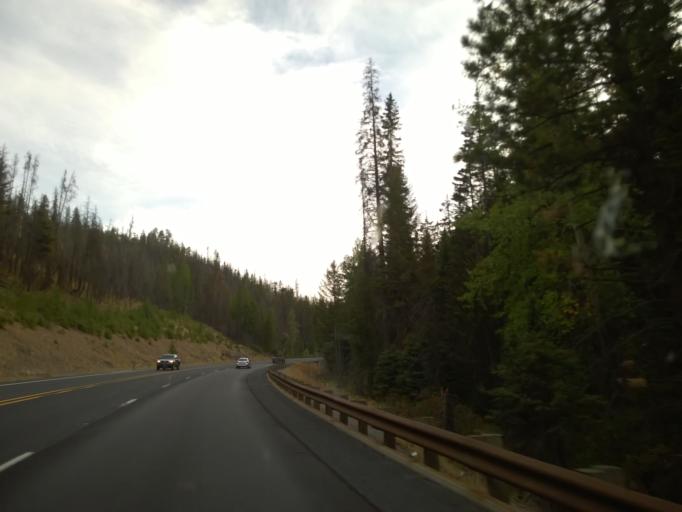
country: US
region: Washington
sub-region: Chelan County
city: Cashmere
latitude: 47.3562
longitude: -120.5635
